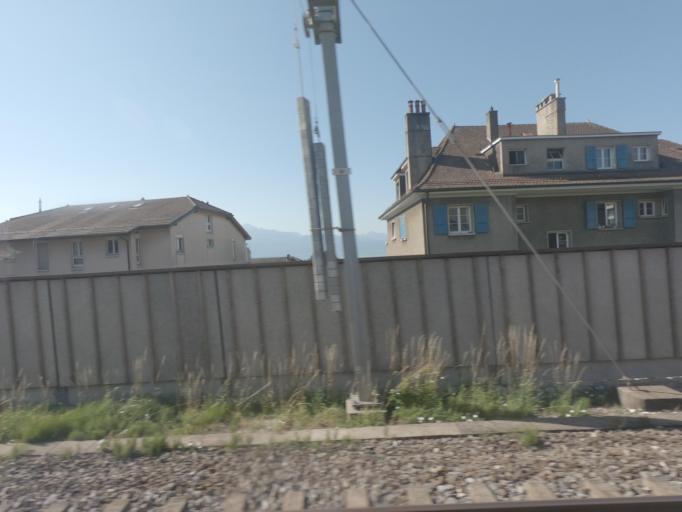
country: CH
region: Vaud
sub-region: Lavaux-Oron District
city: Pully
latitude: 46.5112
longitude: 6.6543
